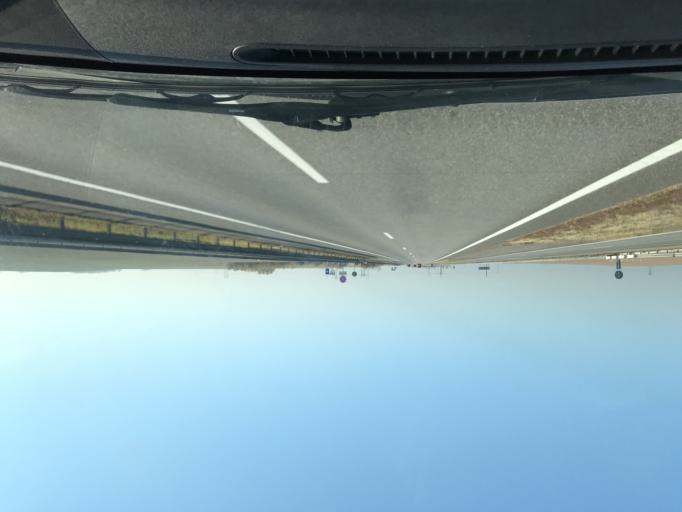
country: BY
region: Vitebsk
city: Talachyn
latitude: 54.4493
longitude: 29.6589
